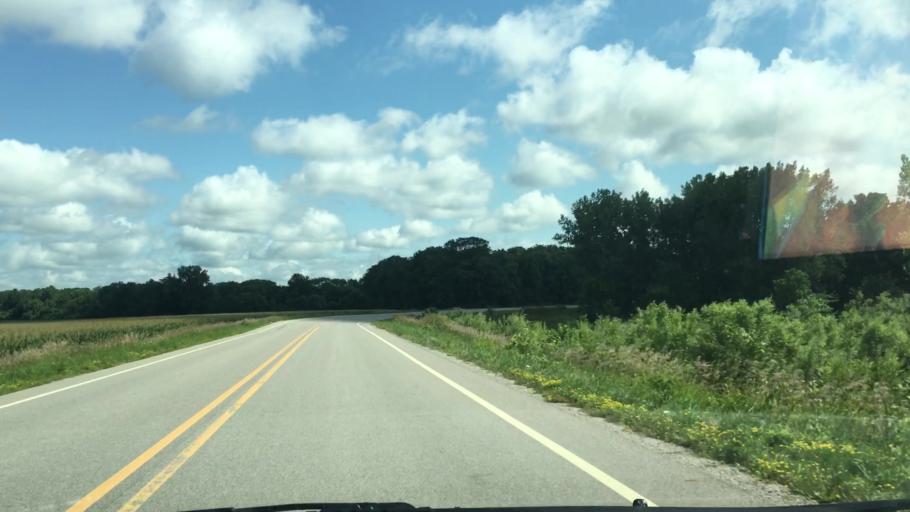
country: US
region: Iowa
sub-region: Linn County
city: Lisbon
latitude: 41.8430
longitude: -91.3960
